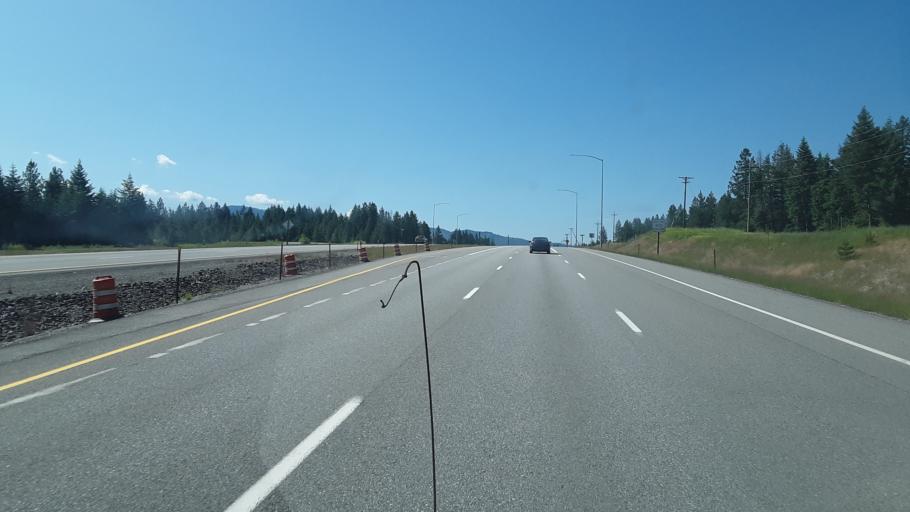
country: US
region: Idaho
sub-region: Kootenai County
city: Spirit Lake
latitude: 47.9809
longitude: -116.6982
